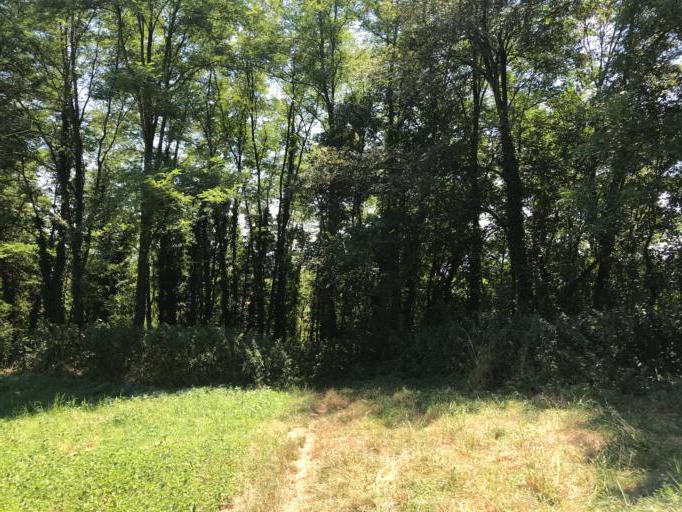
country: FR
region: Rhone-Alpes
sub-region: Departement de l'Ain
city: Saint-Maurice-de-Beynost
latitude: 45.8380
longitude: 4.9828
